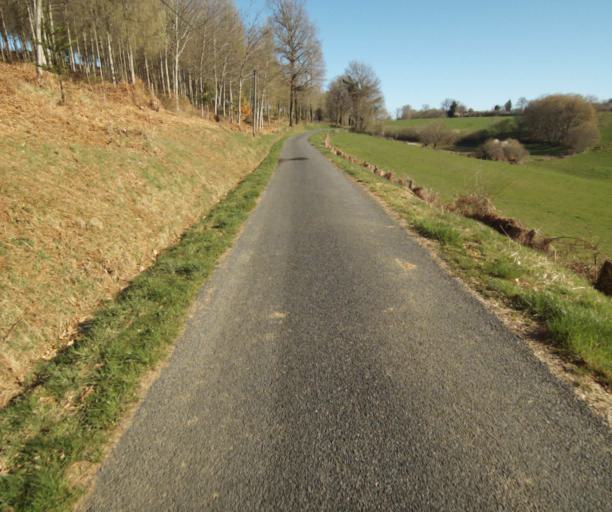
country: FR
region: Limousin
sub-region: Departement de la Correze
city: Seilhac
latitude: 45.3798
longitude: 1.7590
